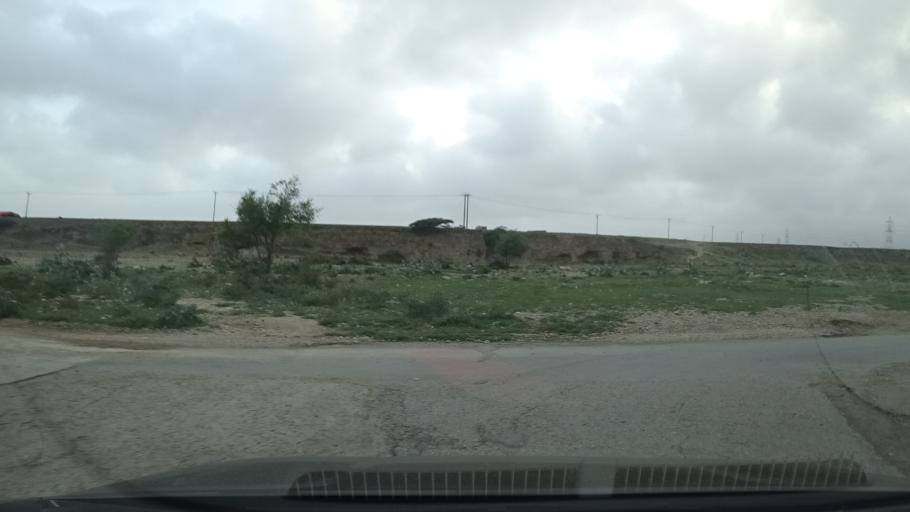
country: OM
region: Zufar
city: Salalah
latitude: 17.1015
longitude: 54.2332
